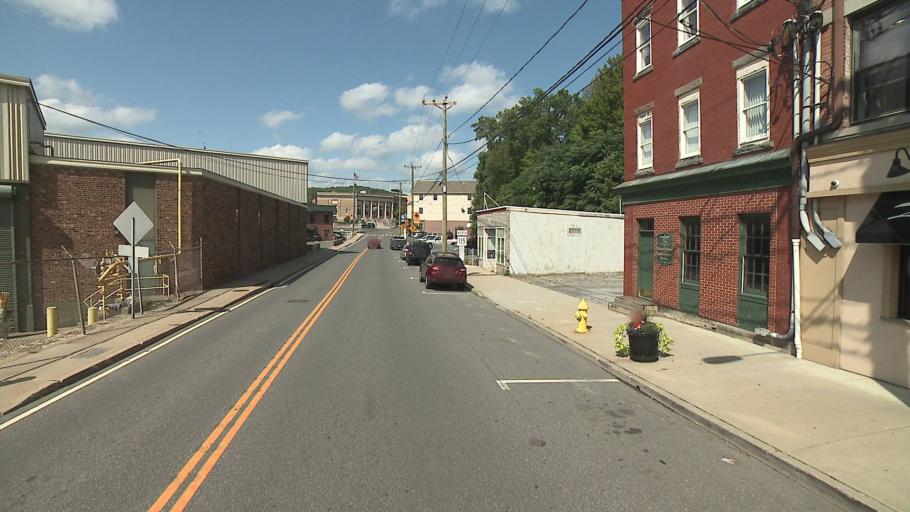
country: US
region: Connecticut
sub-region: New Haven County
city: Seymour
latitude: 41.3930
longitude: -73.0734
